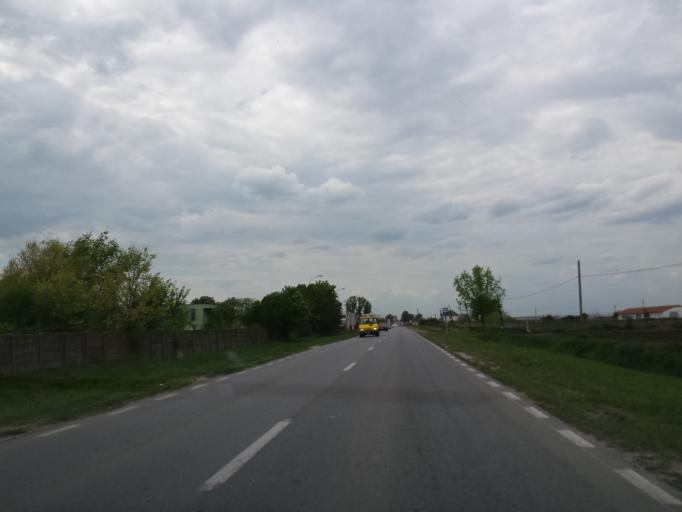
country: RO
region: Timis
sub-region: Comuna Sanpetru Mare
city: Sanpetru Mare
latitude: 46.0497
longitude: 20.6478
